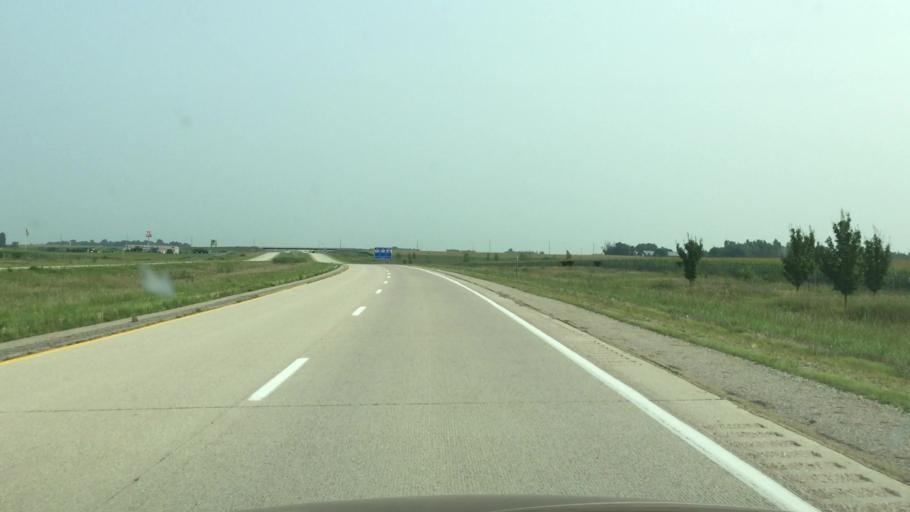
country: US
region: Iowa
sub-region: Osceola County
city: Sibley
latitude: 43.3944
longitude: -95.7176
